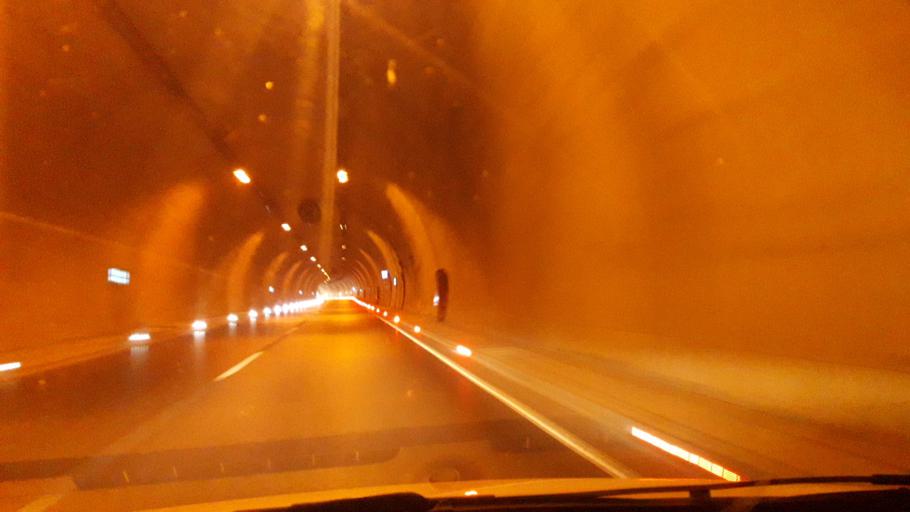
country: TR
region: Sinop
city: Gerze
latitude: 41.7396
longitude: 35.2547
